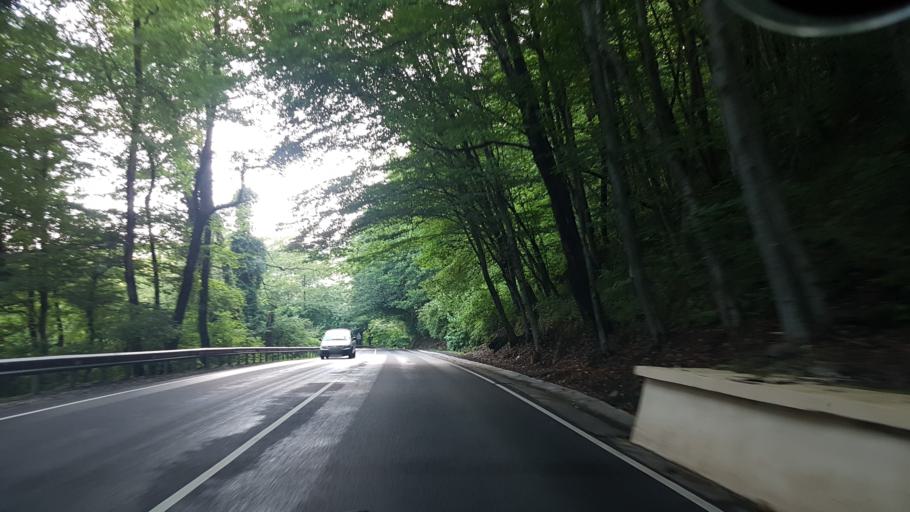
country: RU
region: Krasnodarskiy
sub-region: Sochi City
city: Lazarevskoye
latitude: 43.8751
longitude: 39.4002
